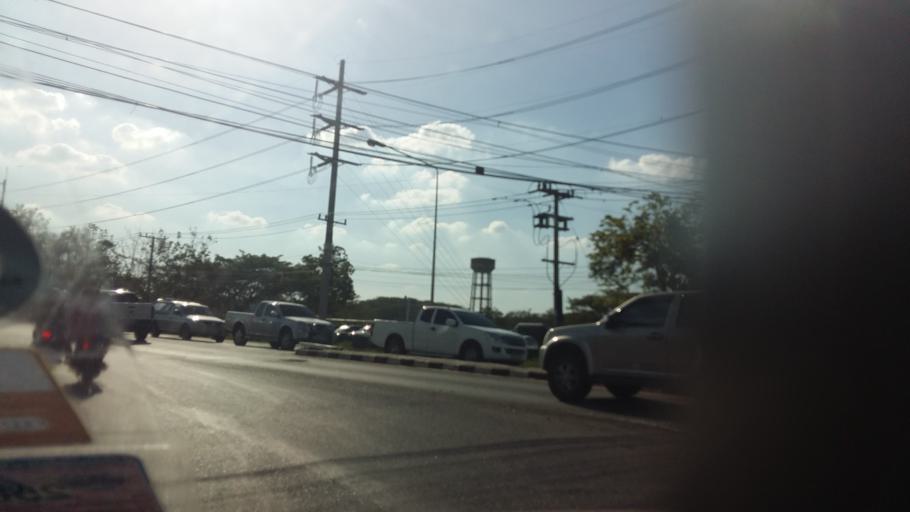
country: TH
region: Lop Buri
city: Lop Buri
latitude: 14.8456
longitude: 100.6427
